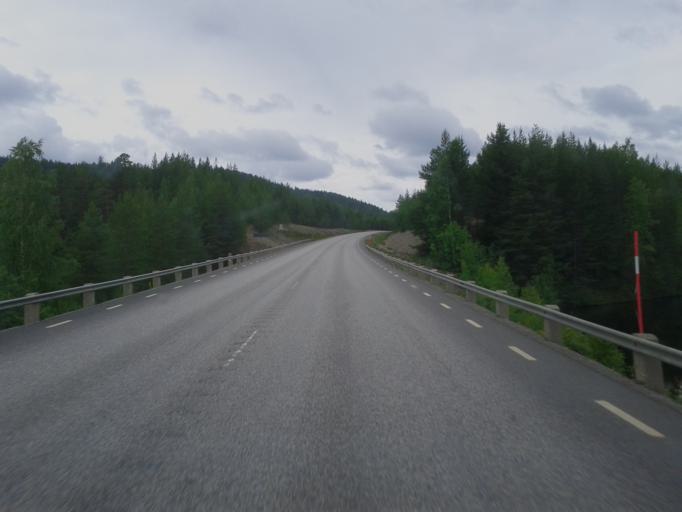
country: SE
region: Vaesterbotten
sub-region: Skelleftea Kommun
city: Langsele
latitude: 64.9204
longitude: 20.0705
